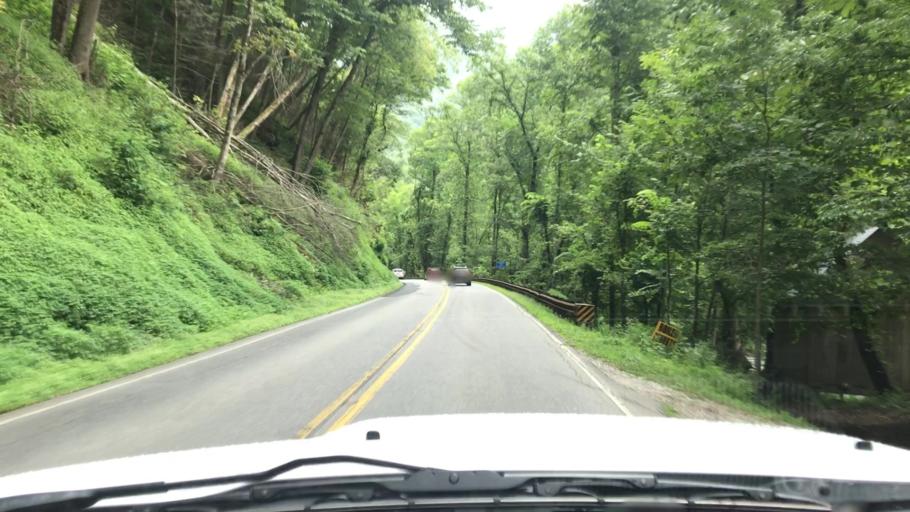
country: US
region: North Carolina
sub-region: Graham County
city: Robbinsville
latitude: 35.3358
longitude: -83.6183
